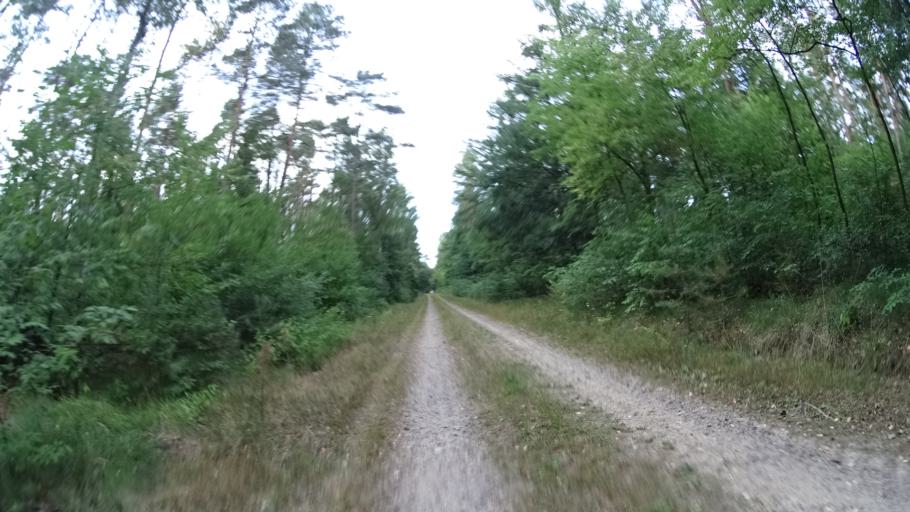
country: DE
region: Lower Saxony
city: Handeloh
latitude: 53.2071
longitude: 9.8807
